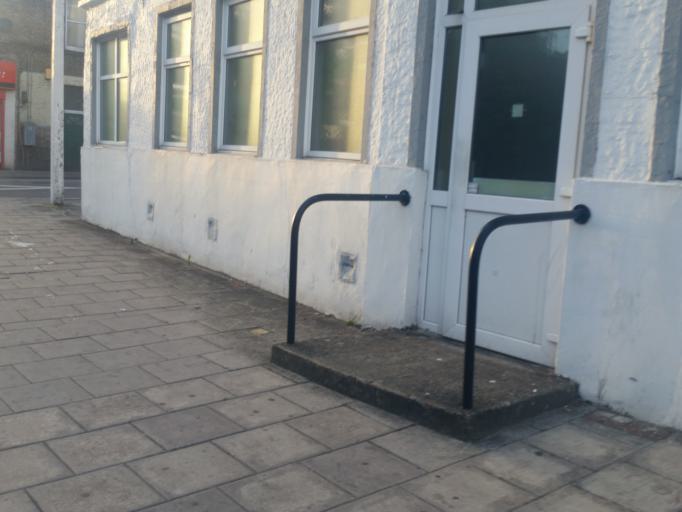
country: GB
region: England
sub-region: Greater London
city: Harringay
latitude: 51.5862
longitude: -0.0945
